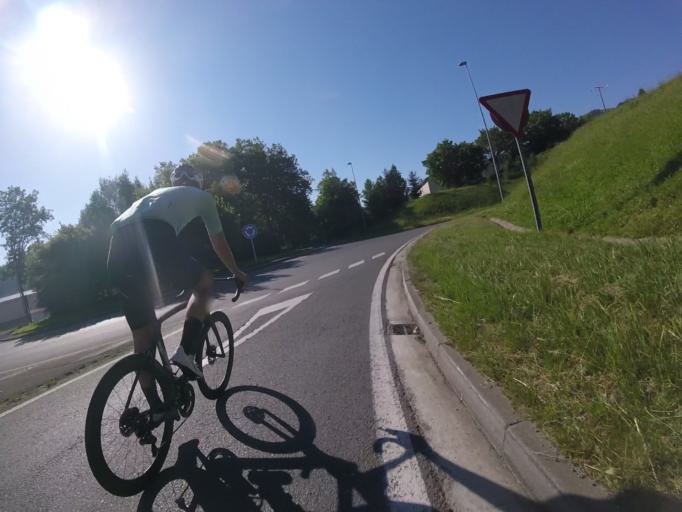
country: ES
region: Basque Country
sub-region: Provincia de Guipuzcoa
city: Azpeitia
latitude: 43.1730
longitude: -2.2568
